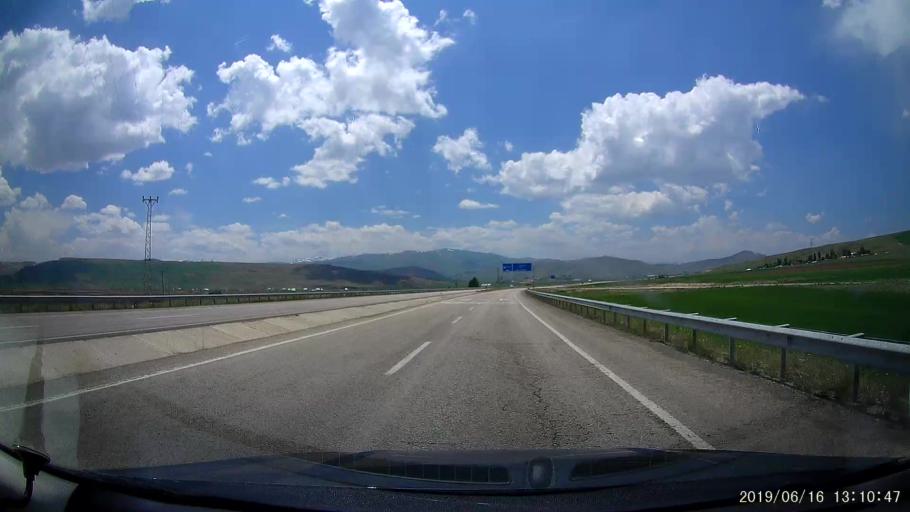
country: TR
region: Agri
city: Diyadin
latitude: 39.5923
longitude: 43.6242
